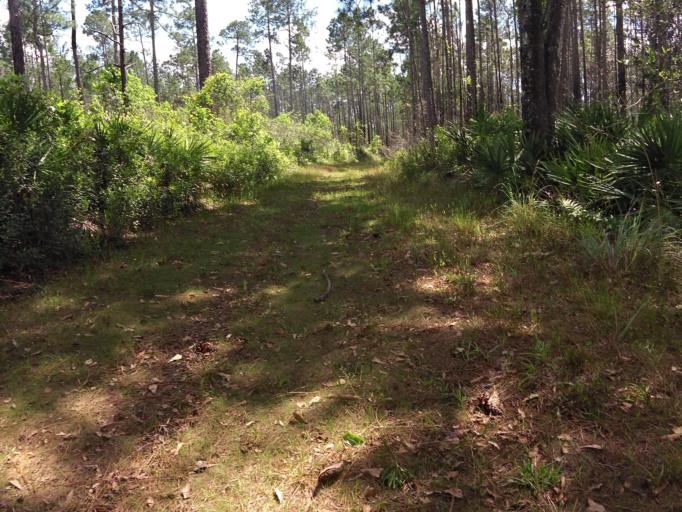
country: US
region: Florida
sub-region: Clay County
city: Green Cove Springs
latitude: 29.9693
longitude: -81.6399
